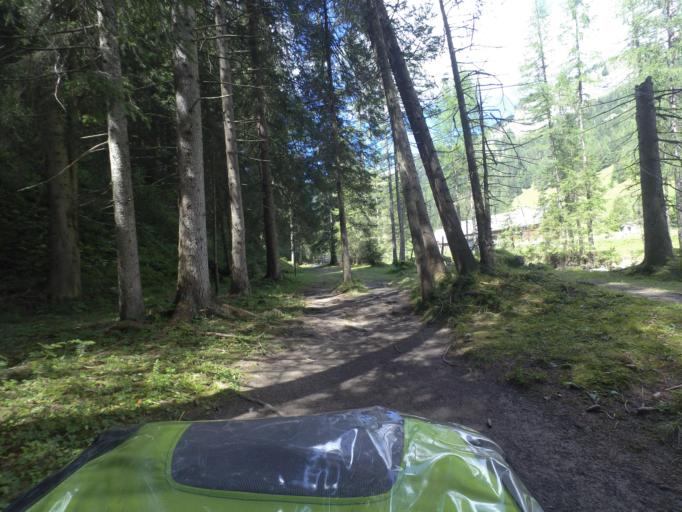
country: AT
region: Salzburg
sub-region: Politischer Bezirk Sankt Johann im Pongau
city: Kleinarl
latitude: 47.1858
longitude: 13.3829
